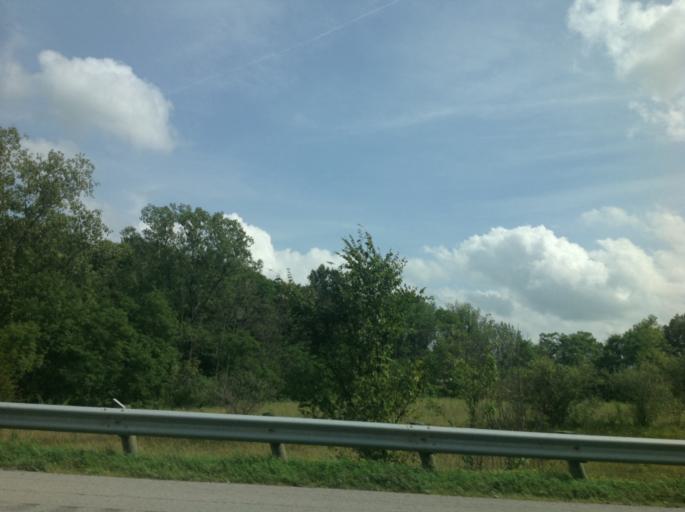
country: US
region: Ohio
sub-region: Richland County
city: Lexington
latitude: 40.5729
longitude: -82.6124
